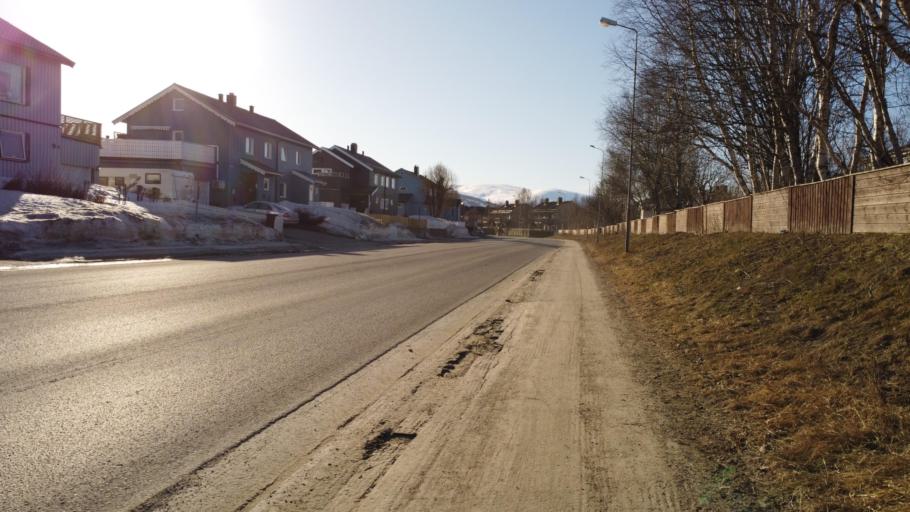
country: NO
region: Nordland
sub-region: Rana
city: Mo i Rana
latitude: 66.3191
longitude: 14.1901
